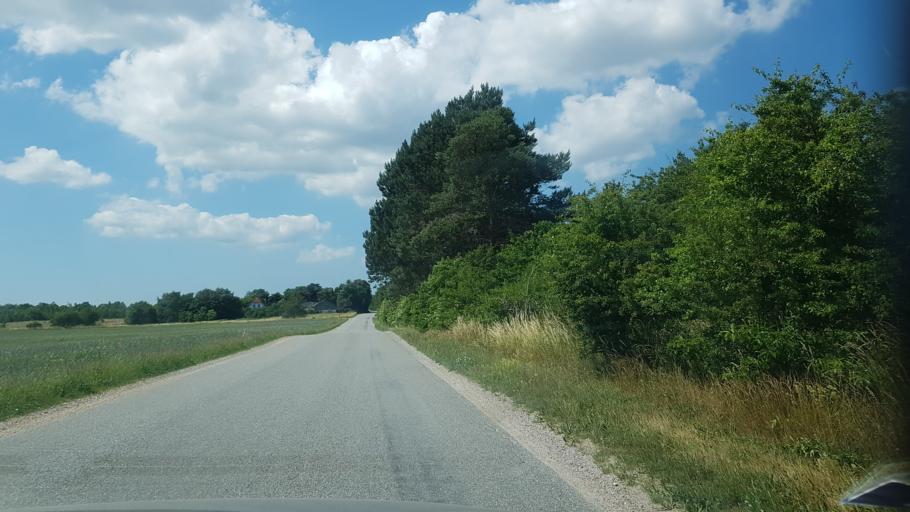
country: DK
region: Zealand
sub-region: Kalundborg Kommune
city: Svebolle
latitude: 55.6902
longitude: 11.2617
